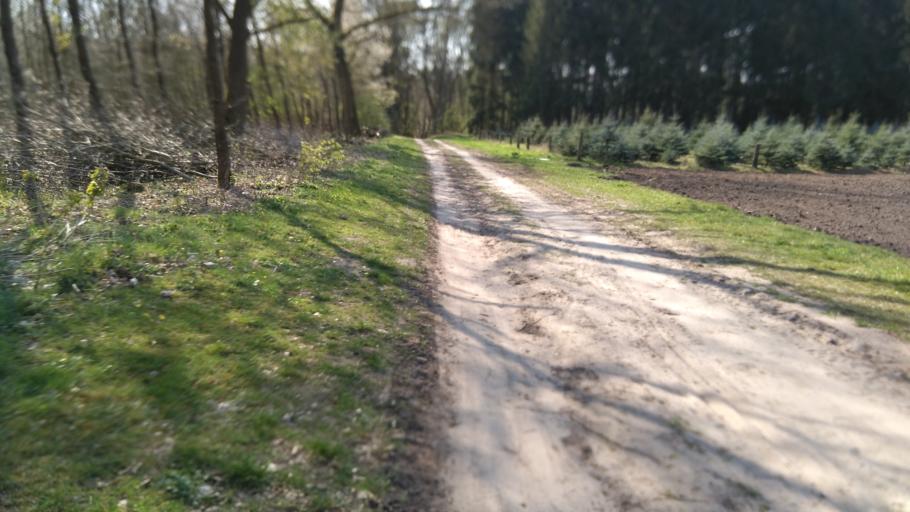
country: DE
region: Lower Saxony
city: Harsefeld
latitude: 53.4749
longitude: 9.5297
